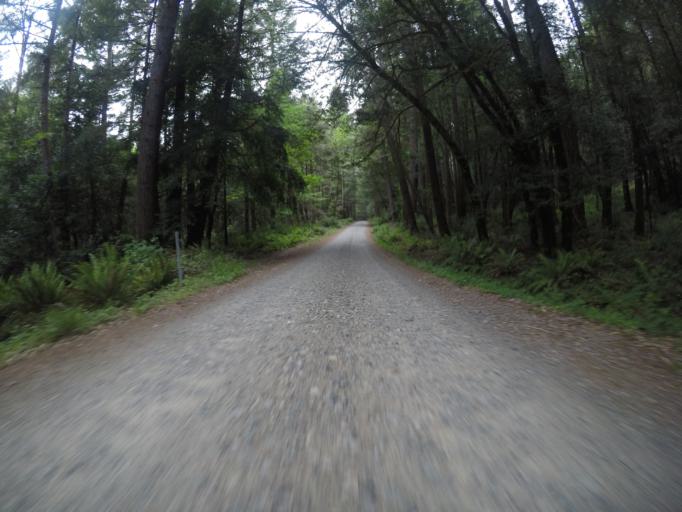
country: US
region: California
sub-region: Del Norte County
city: Bertsch-Oceanview
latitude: 41.7008
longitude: -123.8986
